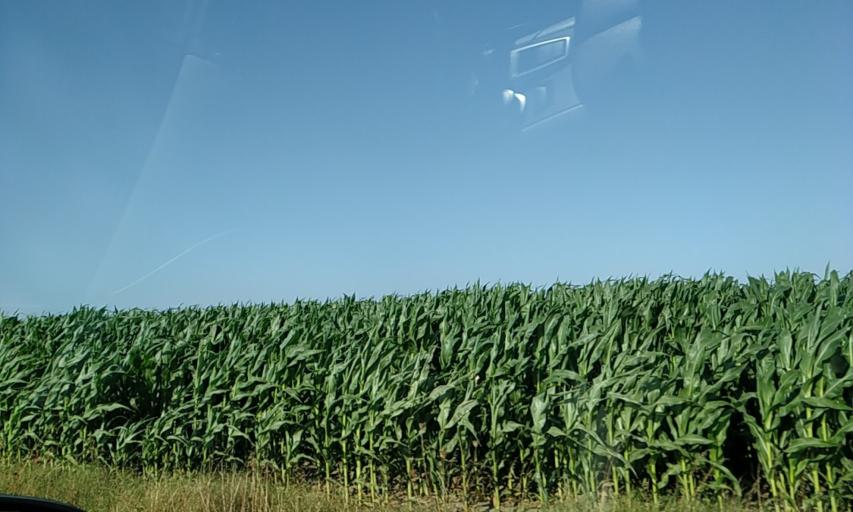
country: PT
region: Santarem
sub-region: Almeirim
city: Fazendas de Almeirim
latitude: 39.1540
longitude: -8.6196
